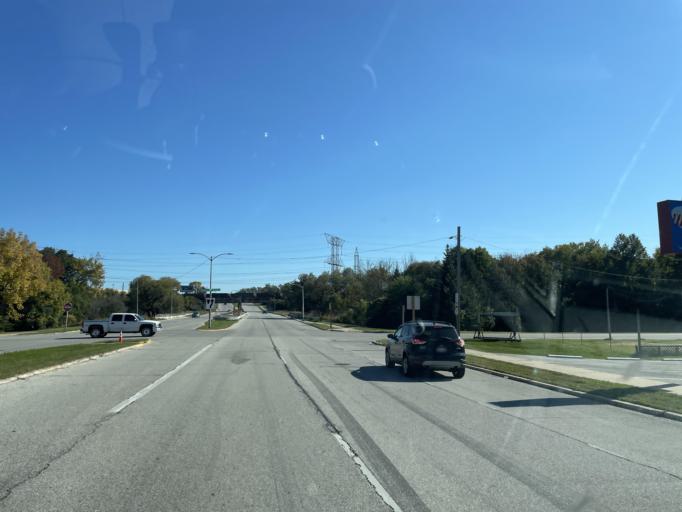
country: US
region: Wisconsin
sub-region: Waukesha County
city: Butler
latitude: 43.1255
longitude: -88.0433
